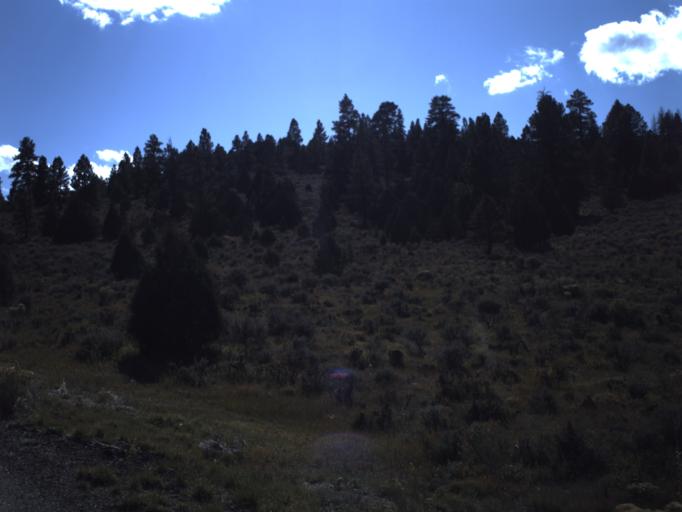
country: US
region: Utah
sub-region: Garfield County
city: Panguitch
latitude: 37.7402
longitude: -112.5907
